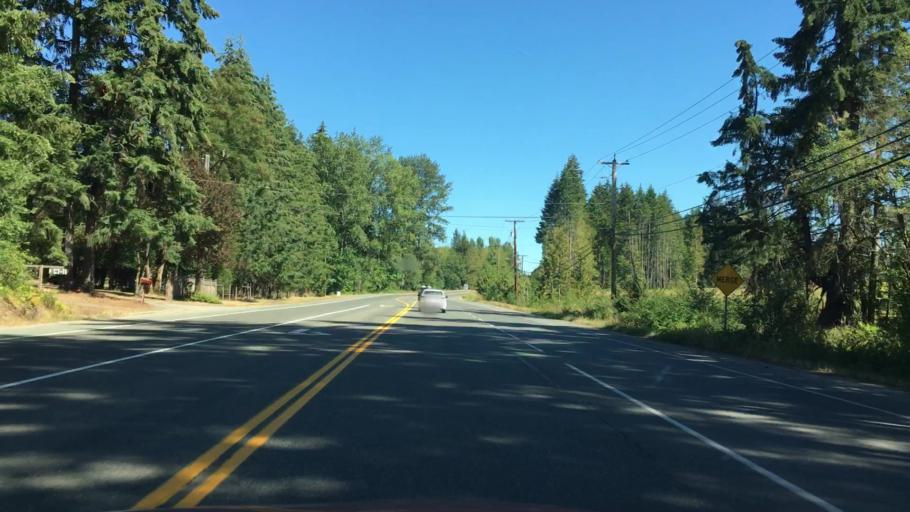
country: CA
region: British Columbia
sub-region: Regional District of Nanaimo
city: Parksville
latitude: 49.3104
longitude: -124.4984
